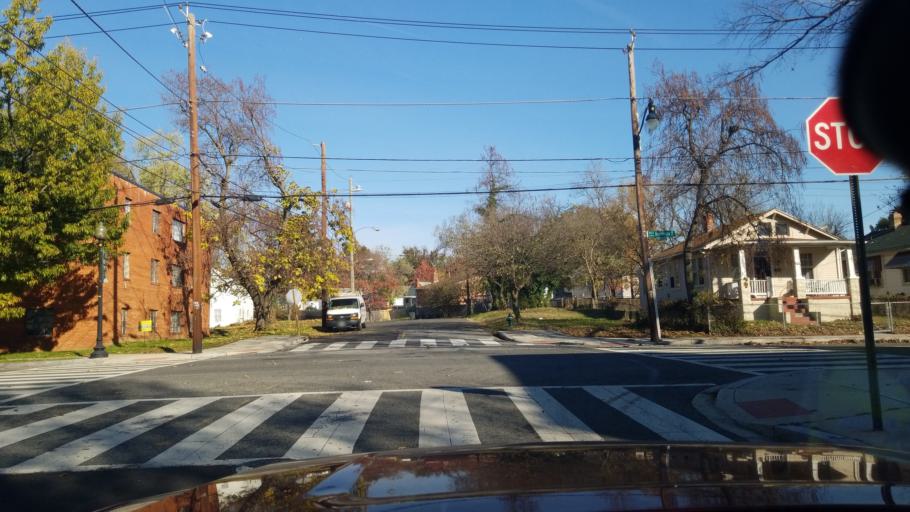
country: US
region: Maryland
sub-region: Prince George's County
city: Fairmount Heights
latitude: 38.8982
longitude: -76.9205
